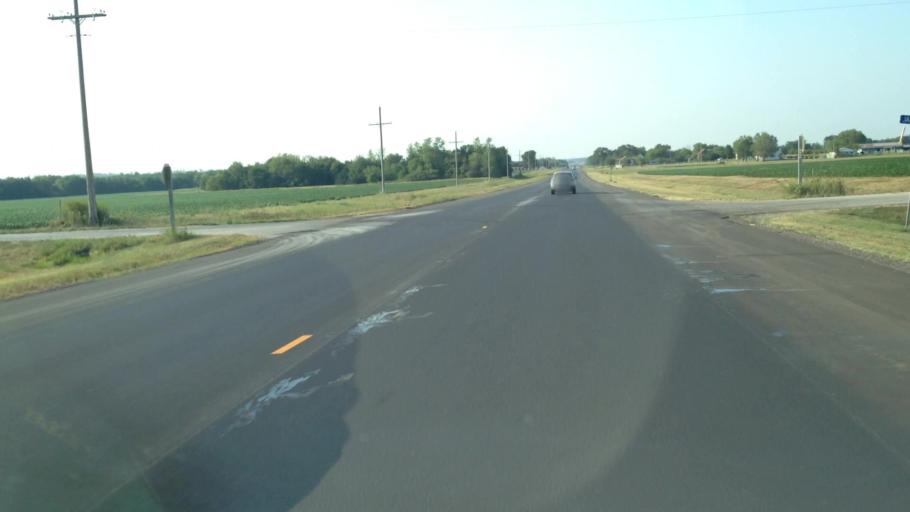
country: US
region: Kansas
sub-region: Franklin County
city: Ottawa
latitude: 38.5353
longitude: -95.2677
